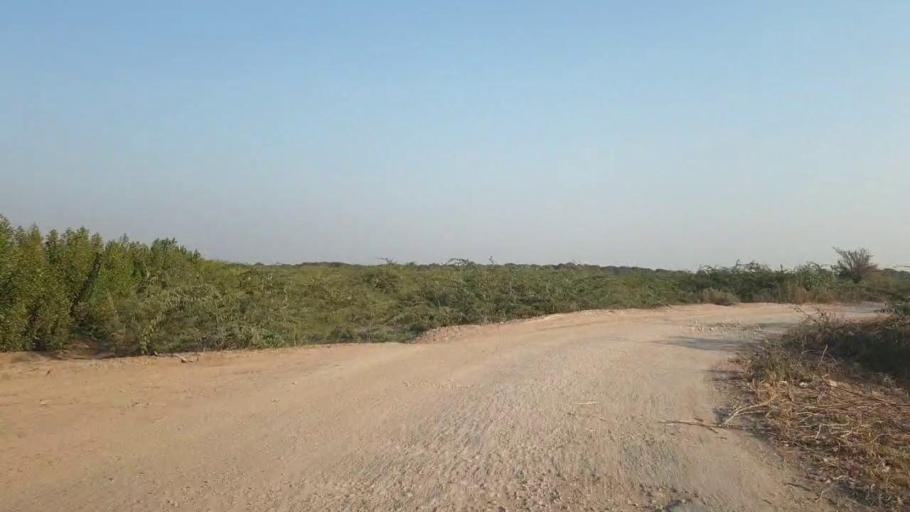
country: PK
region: Sindh
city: Mirpur Khas
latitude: 25.4224
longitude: 68.9066
